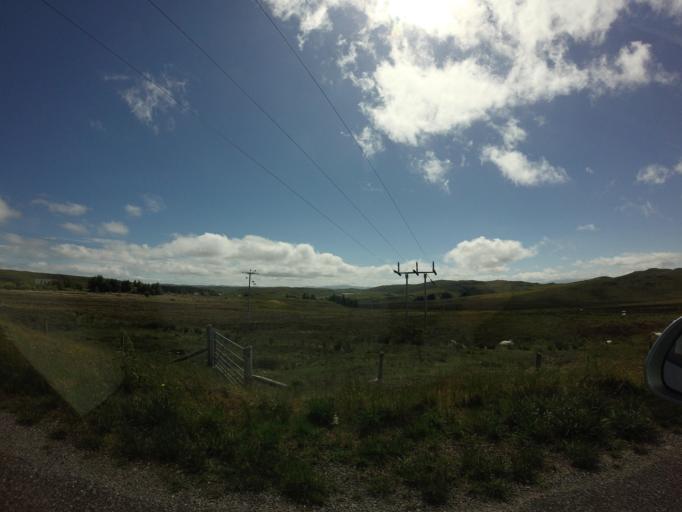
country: GB
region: Scotland
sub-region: Eilean Siar
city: Stornoway
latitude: 58.1546
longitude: -6.5036
